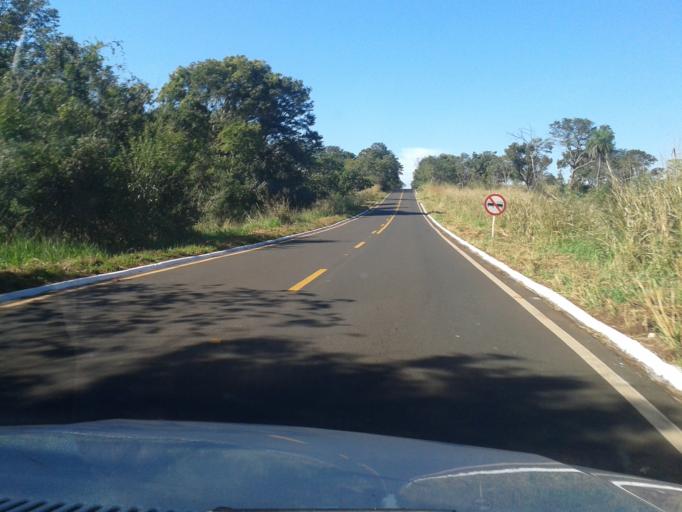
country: BR
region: Minas Gerais
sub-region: Ituiutaba
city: Ituiutaba
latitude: -19.0242
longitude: -49.7736
